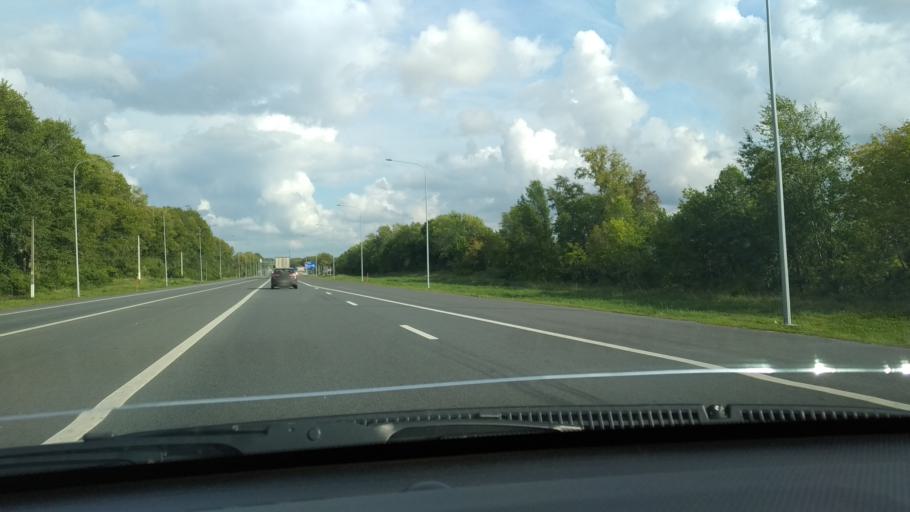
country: RU
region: Tatarstan
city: Stolbishchi
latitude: 55.6587
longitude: 49.3043
